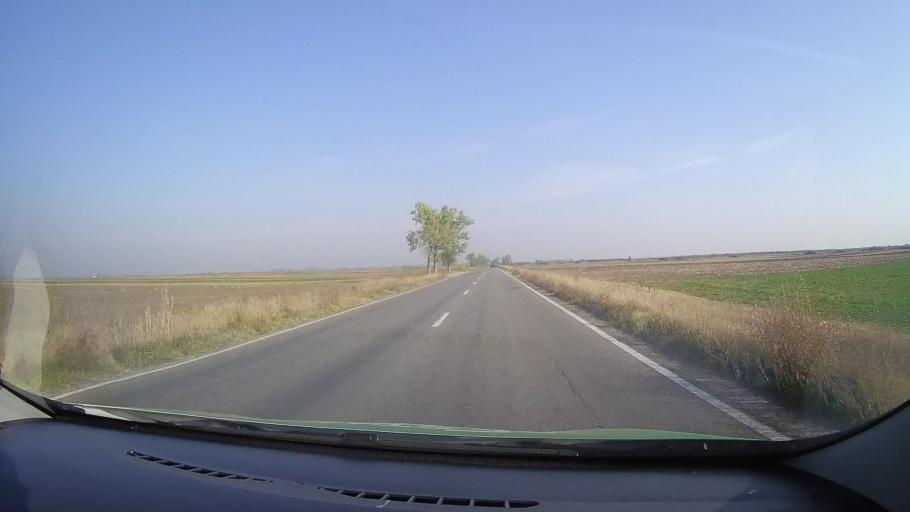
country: RO
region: Arad
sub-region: Comuna Pilu
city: Pilu
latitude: 46.5909
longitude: 21.3464
